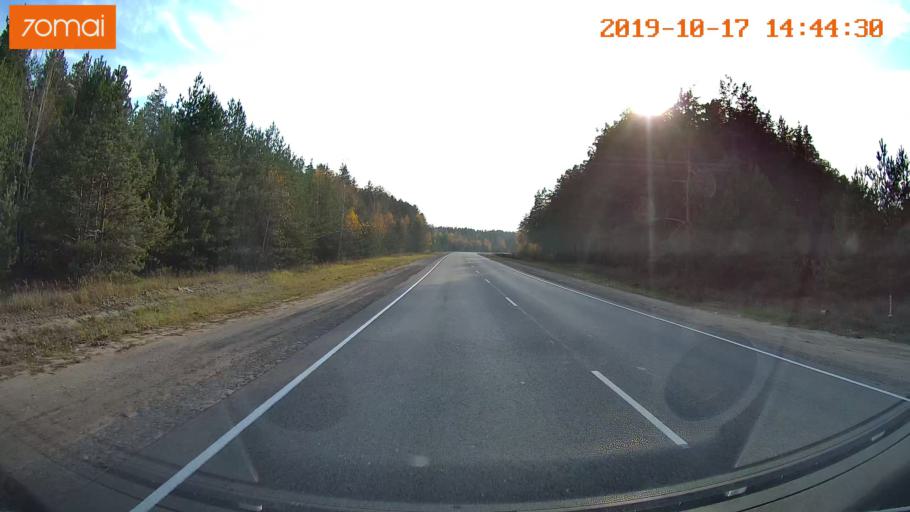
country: RU
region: Rjazan
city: Solotcha
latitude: 54.8121
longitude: 39.8911
